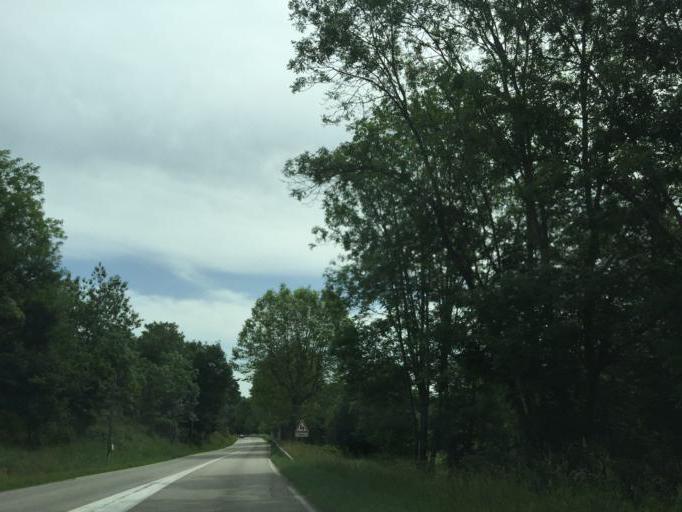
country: FR
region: Rhone-Alpes
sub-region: Departement de l'Ardeche
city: Saint-Marcel-les-Annonay
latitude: 45.2921
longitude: 4.6036
